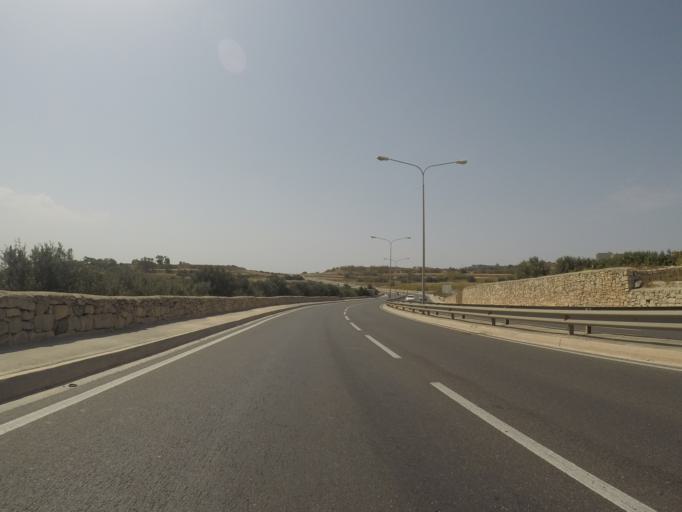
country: MT
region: L-Imdina
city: Imdina
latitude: 35.8897
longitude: 14.4100
